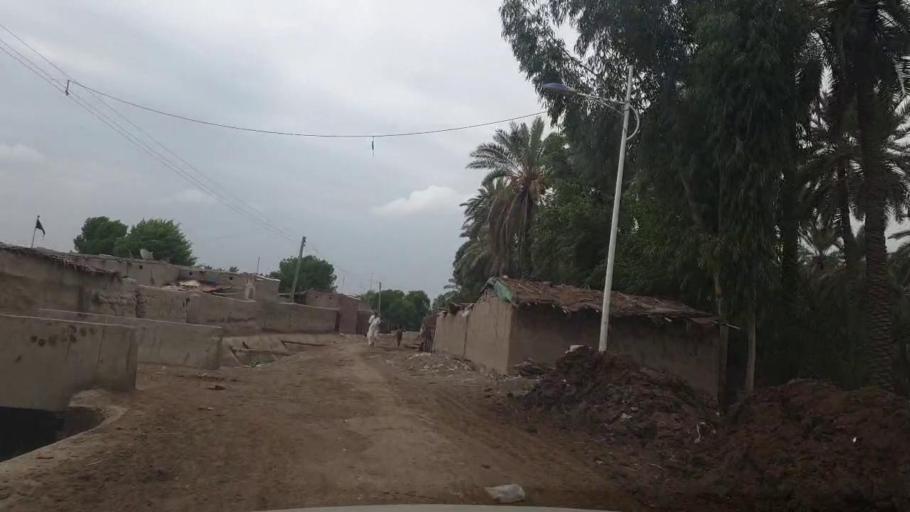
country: PK
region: Sindh
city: Khairpur
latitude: 27.6052
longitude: 68.8031
